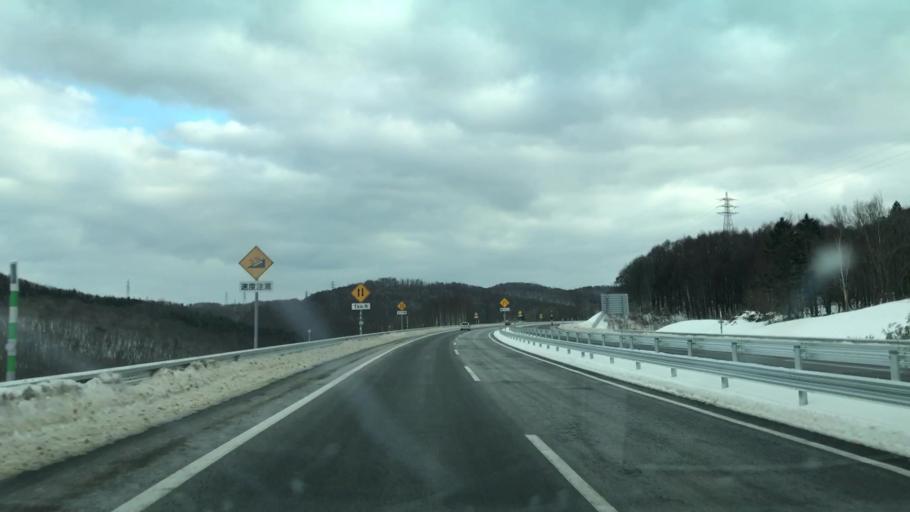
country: JP
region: Hokkaido
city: Otaru
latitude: 43.1999
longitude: 140.9398
